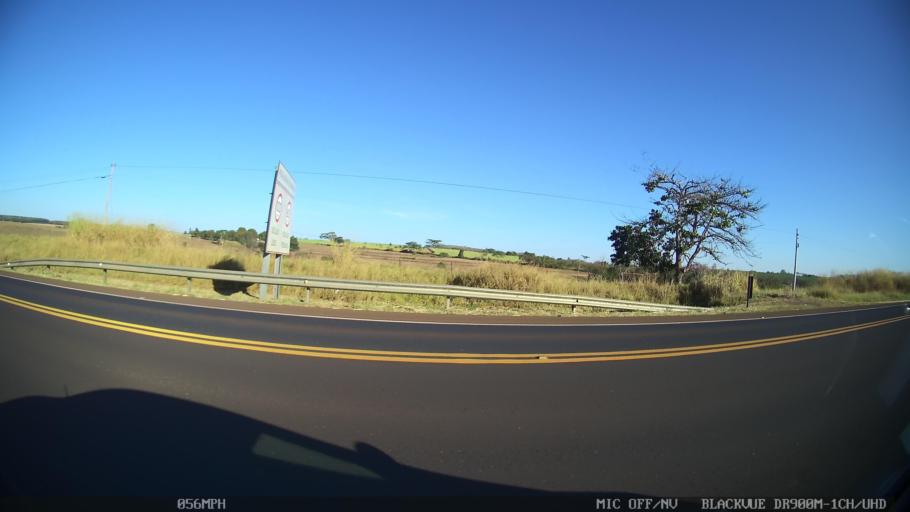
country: BR
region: Sao Paulo
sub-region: Olimpia
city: Olimpia
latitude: -20.7093
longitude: -48.9707
